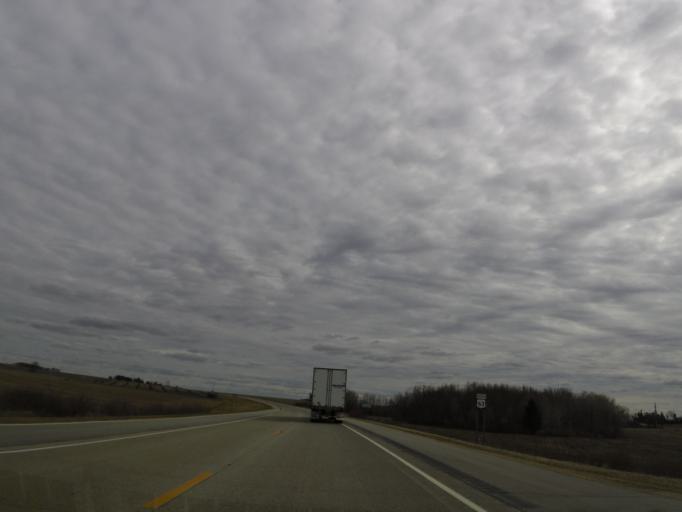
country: US
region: Minnesota
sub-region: Fillmore County
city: Spring Valley
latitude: 43.5586
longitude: -92.3869
